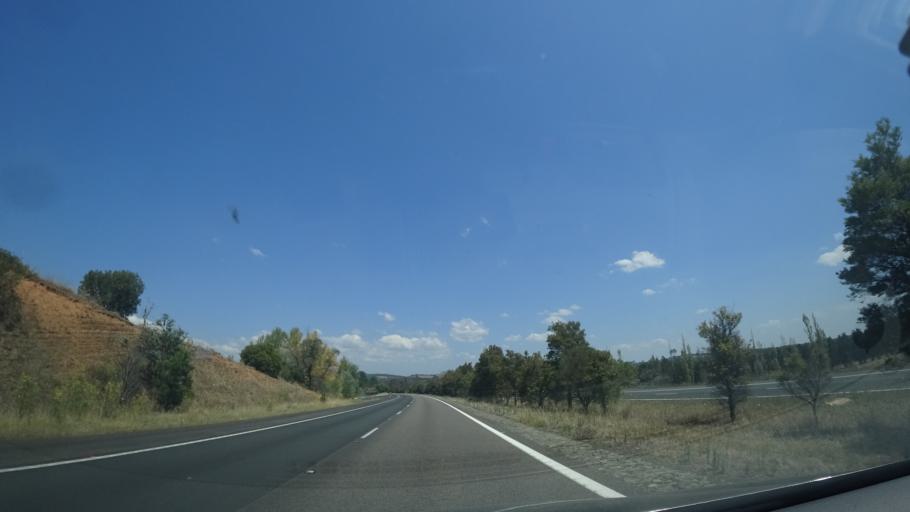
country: AU
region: New South Wales
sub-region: Wingecarribee
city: Bundanoon
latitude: -34.5636
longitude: 150.2555
